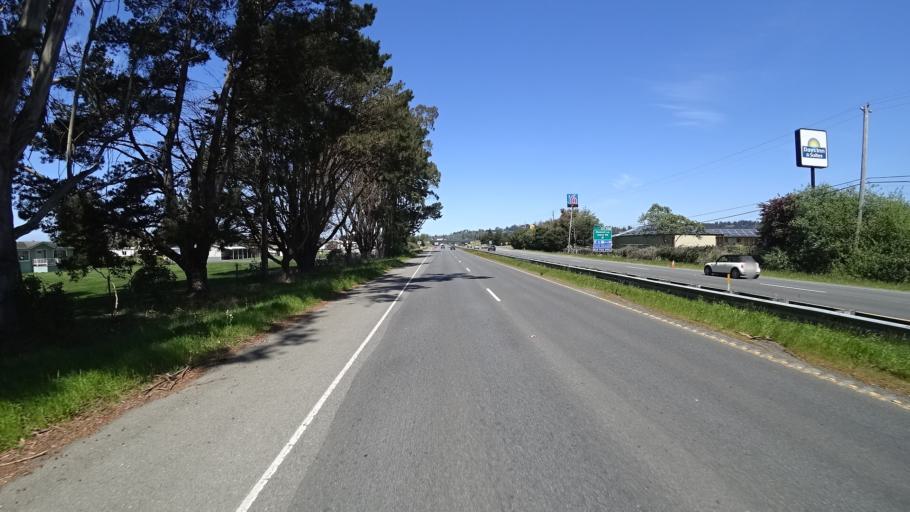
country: US
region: California
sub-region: Humboldt County
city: Arcata
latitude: 40.9005
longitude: -124.0851
